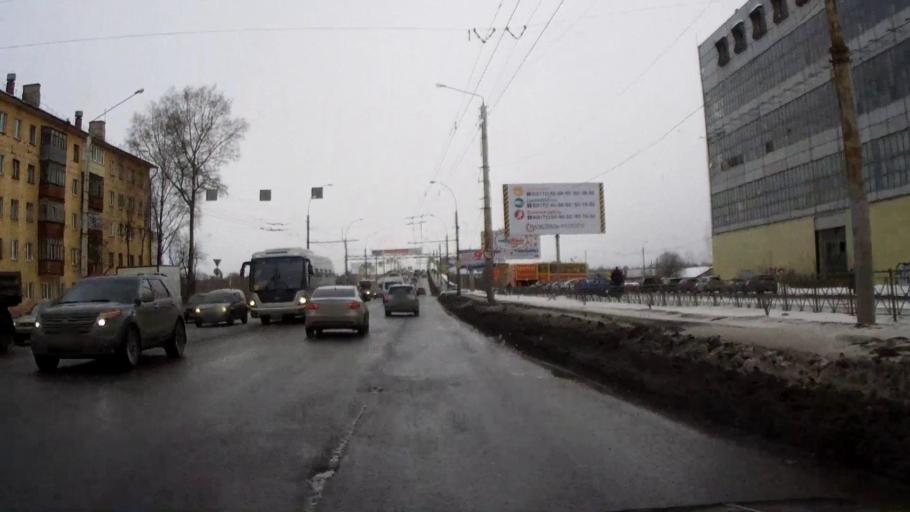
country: RU
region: Vologda
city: Vologda
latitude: 59.2137
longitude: 39.8561
